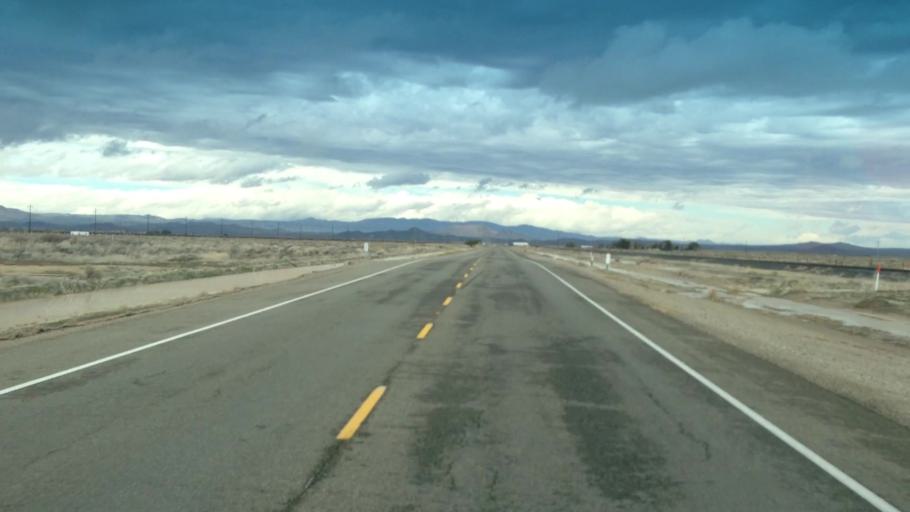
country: US
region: California
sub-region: Los Angeles County
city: Lancaster
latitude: 34.7526
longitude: -118.1453
